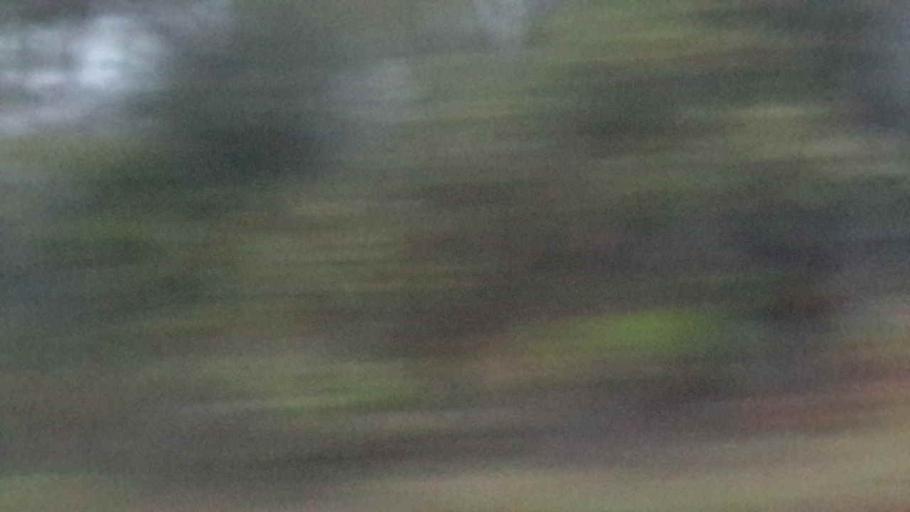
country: AU
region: New South Wales
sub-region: Wollongong
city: Mount Keira
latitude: -34.3952
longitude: 150.8436
